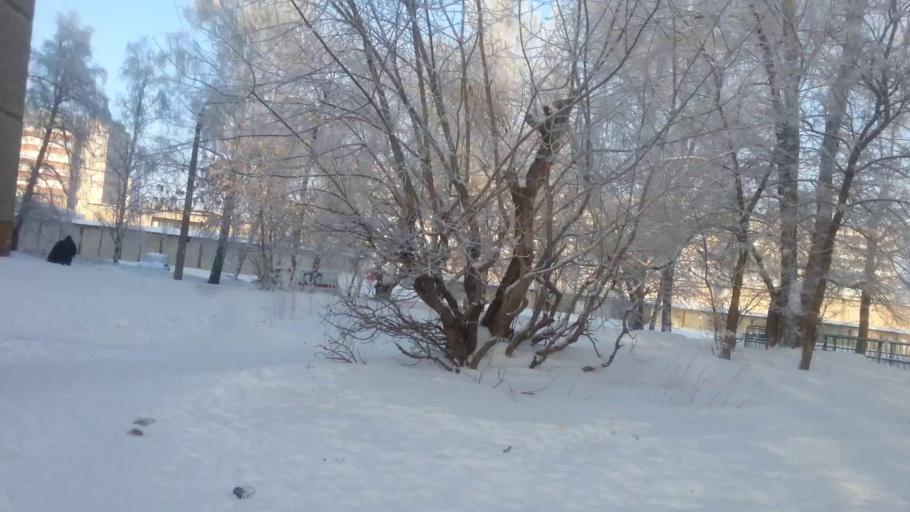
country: RU
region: Altai Krai
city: Novosilikatnyy
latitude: 53.3781
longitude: 83.6732
